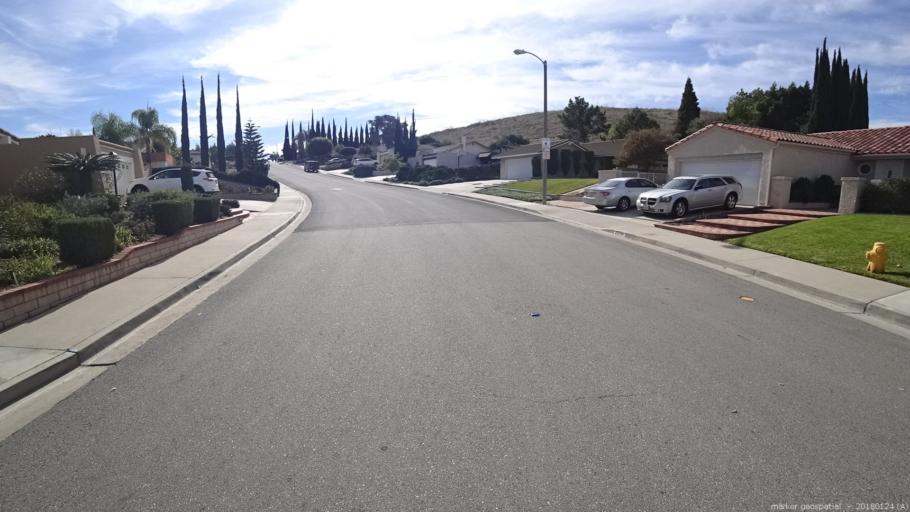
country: US
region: California
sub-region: Los Angeles County
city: Diamond Bar
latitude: 34.0213
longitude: -117.8196
